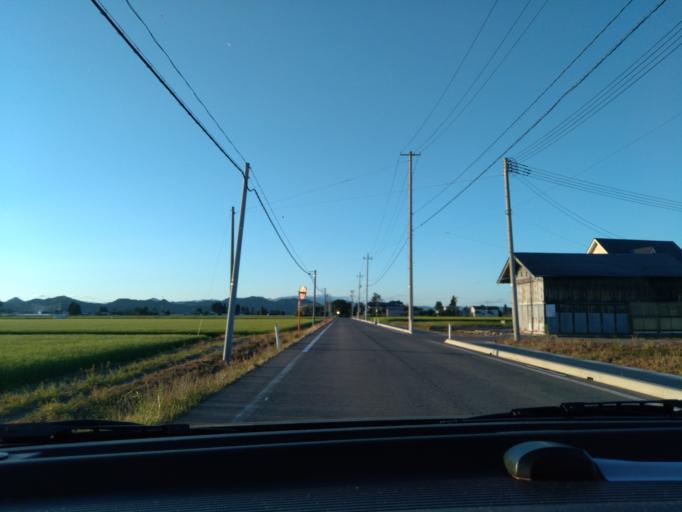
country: JP
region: Akita
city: Omagari
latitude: 39.4847
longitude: 140.5325
